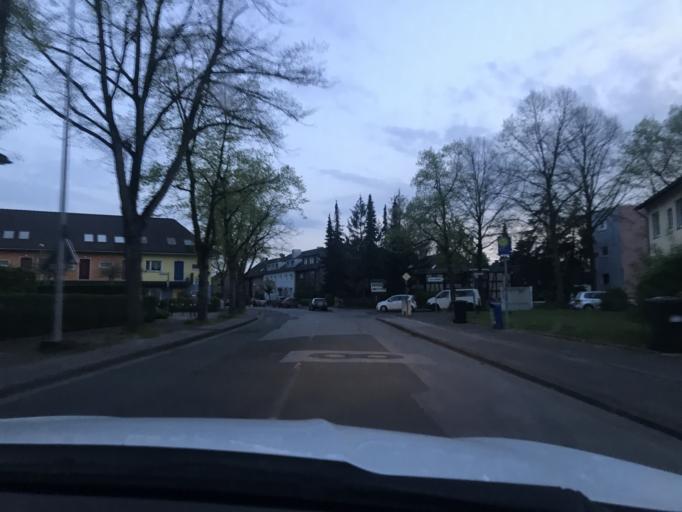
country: DE
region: North Rhine-Westphalia
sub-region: Regierungsbezirk Dusseldorf
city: Hochfeld
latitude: 51.3869
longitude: 6.7049
